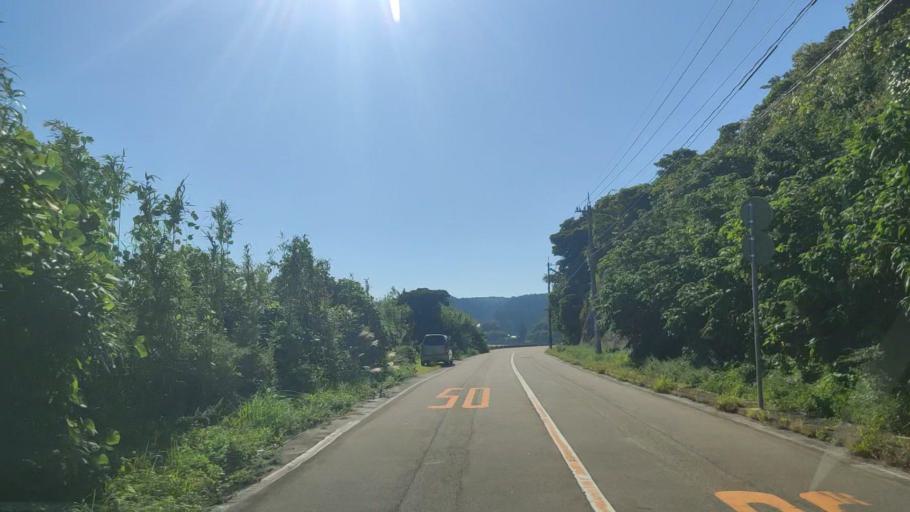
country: JP
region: Ishikawa
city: Nanao
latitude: 37.2799
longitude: 137.1049
